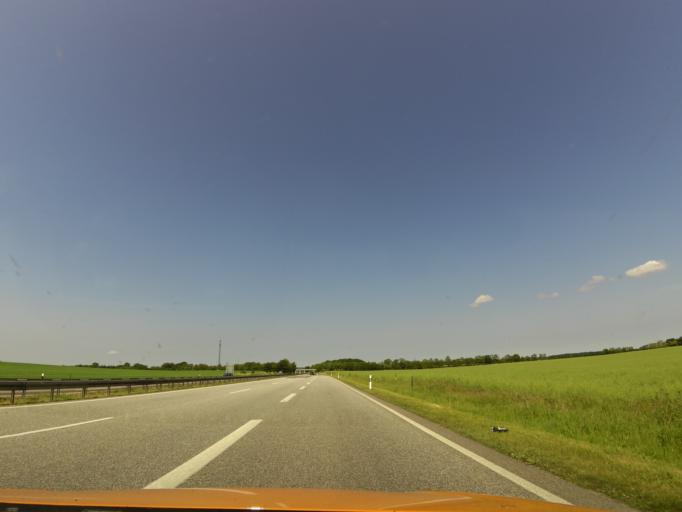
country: DE
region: Brandenburg
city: Gerdshagen
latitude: 53.2649
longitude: 12.1419
